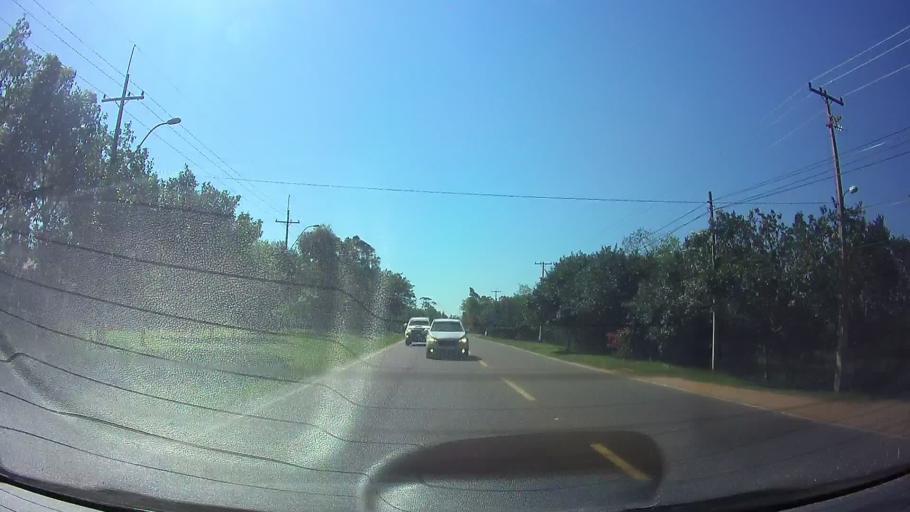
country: PY
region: Cordillera
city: San Bernardino
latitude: -25.3456
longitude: -57.2725
